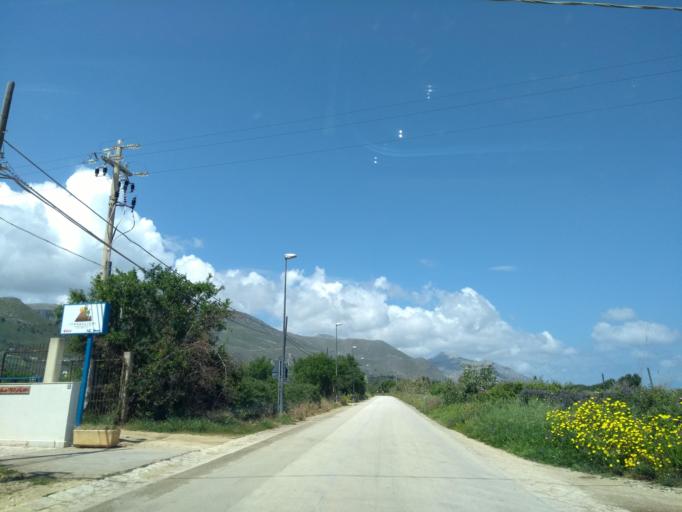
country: IT
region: Sicily
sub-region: Trapani
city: Castellammare del Golfo
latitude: 38.0574
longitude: 12.8334
